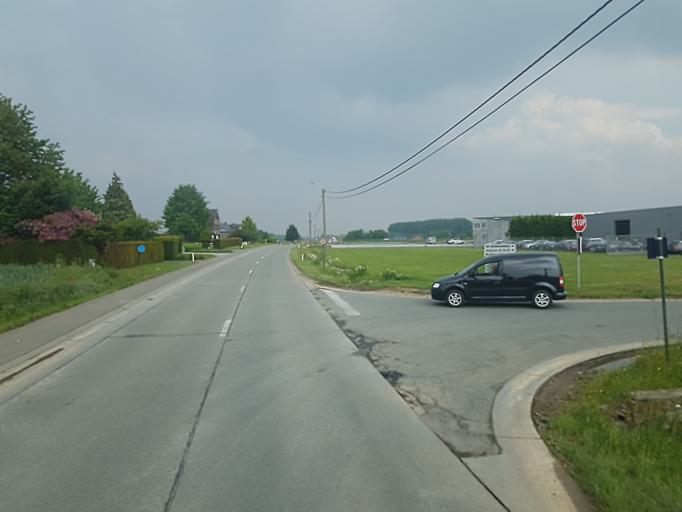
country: BE
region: Flanders
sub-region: Provincie Oost-Vlaanderen
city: Geraardsbergen
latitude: 50.7979
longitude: 3.8821
